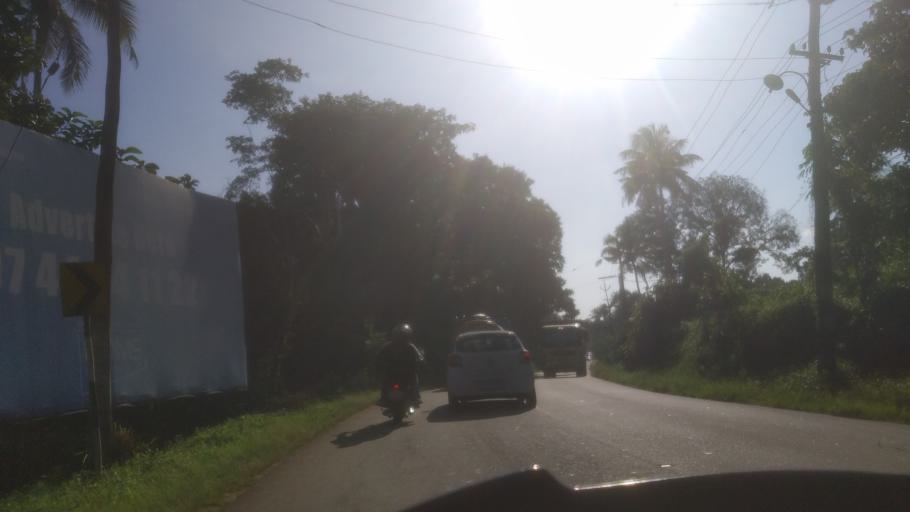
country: IN
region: Kerala
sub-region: Ernakulam
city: Ramamangalam
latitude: 9.9770
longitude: 76.5134
